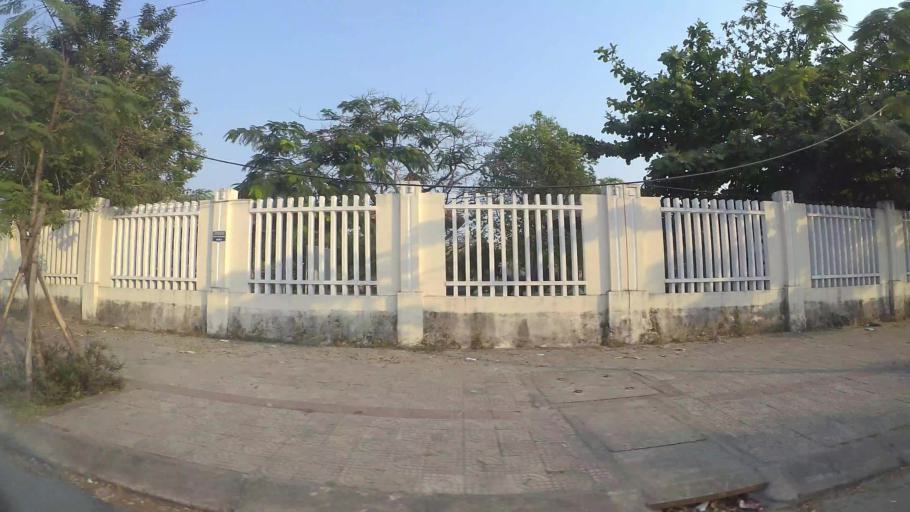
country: VN
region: Da Nang
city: Ngu Hanh Son
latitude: 15.9842
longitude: 108.2388
